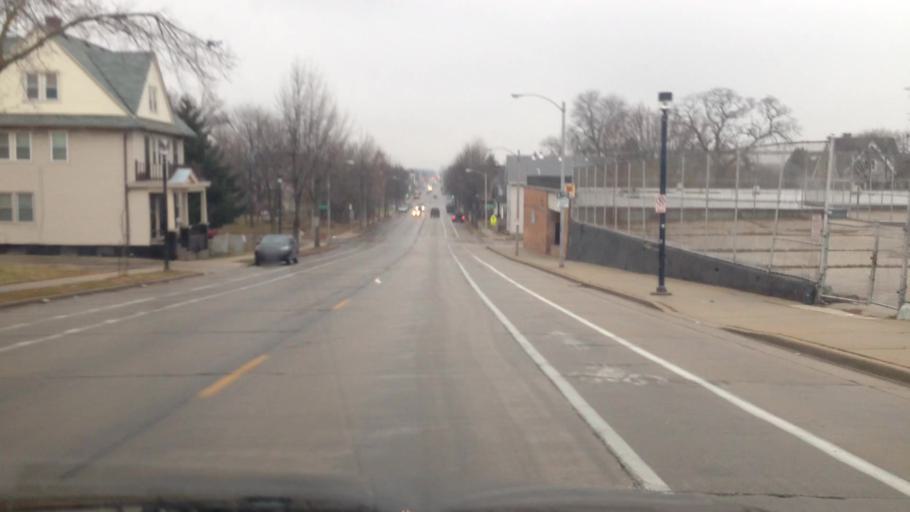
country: US
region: Wisconsin
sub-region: Milwaukee County
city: Milwaukee
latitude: 43.0676
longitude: -87.9098
